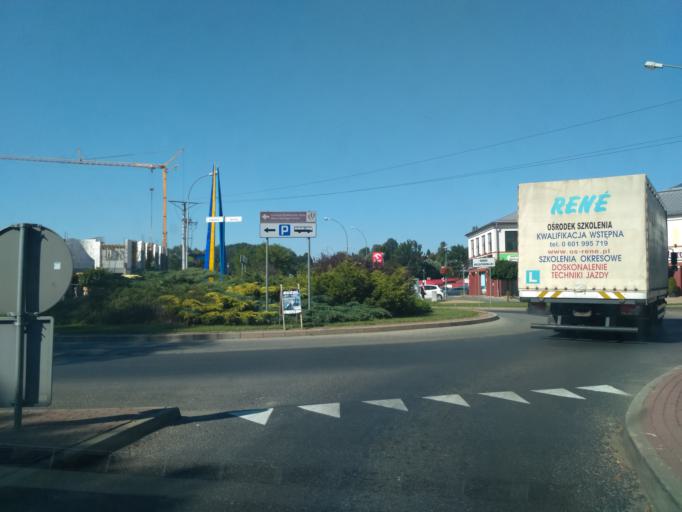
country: PL
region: Subcarpathian Voivodeship
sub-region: Krosno
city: Krosno
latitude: 49.6918
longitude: 21.7730
